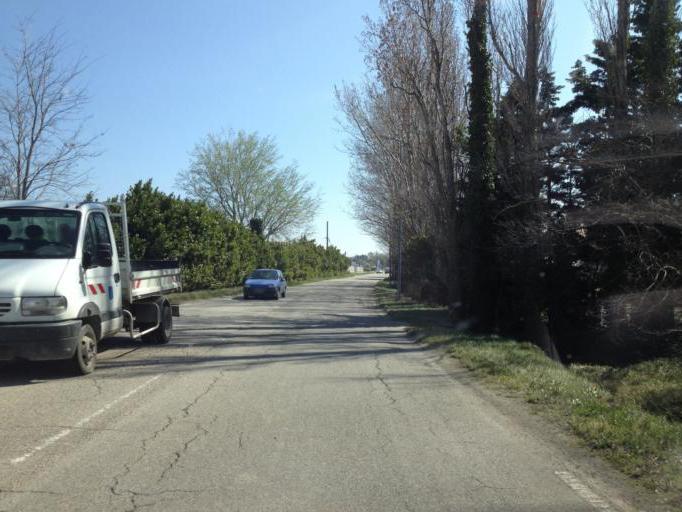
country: FR
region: Provence-Alpes-Cote d'Azur
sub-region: Departement du Vaucluse
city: Jonquieres
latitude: 44.1126
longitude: 4.9104
